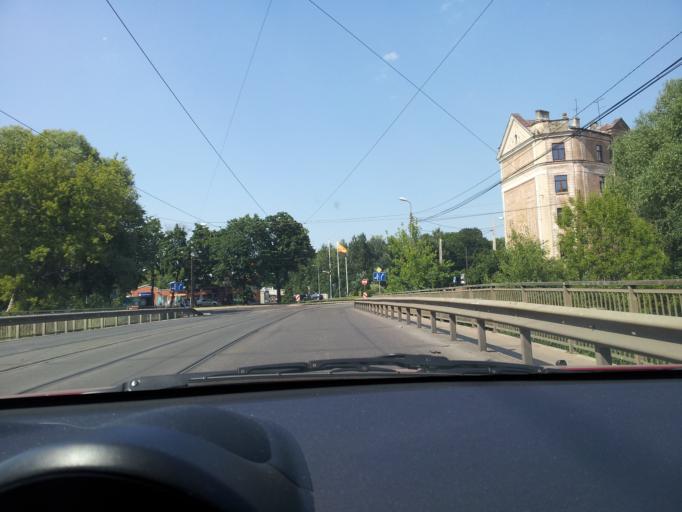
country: LV
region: Riga
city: Riga
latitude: 56.9921
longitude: 24.1225
